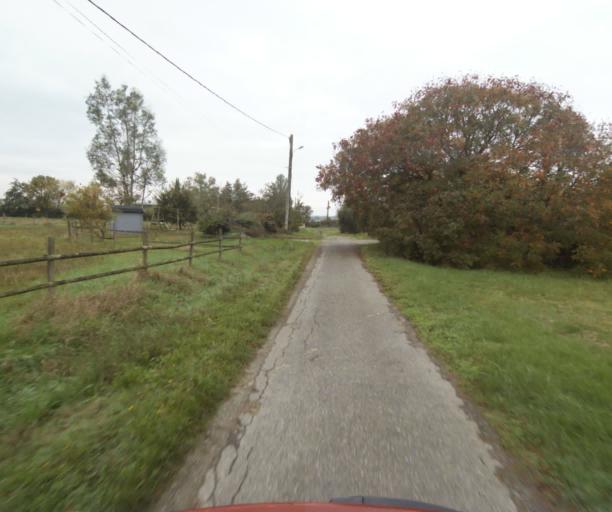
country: FR
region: Midi-Pyrenees
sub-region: Departement du Tarn-et-Garonne
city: Verdun-sur-Garonne
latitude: 43.8621
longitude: 1.2643
